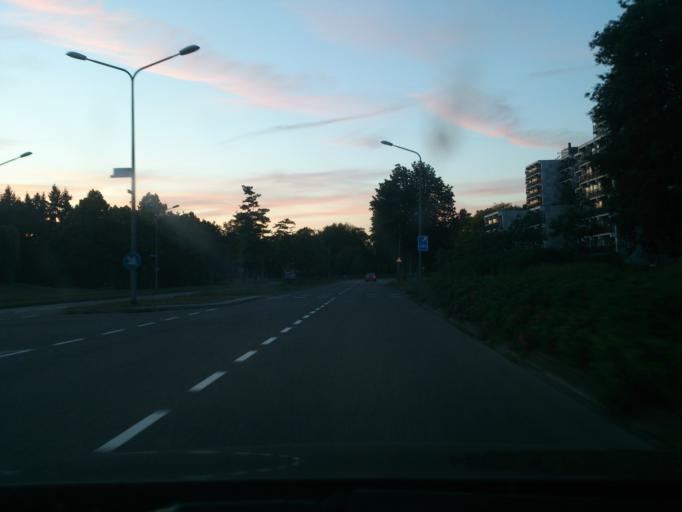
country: NL
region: Gelderland
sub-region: Gemeente Nijmegen
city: Lindenholt
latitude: 51.8145
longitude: 5.8030
